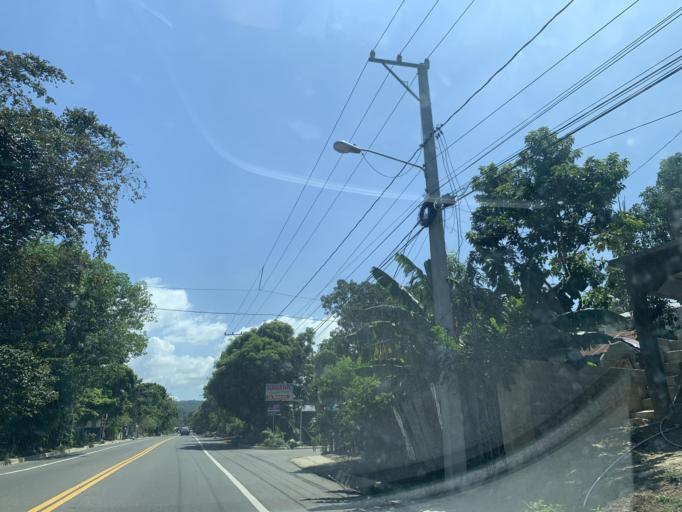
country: DO
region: Puerto Plata
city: Imbert
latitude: 19.7261
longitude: -70.8296
